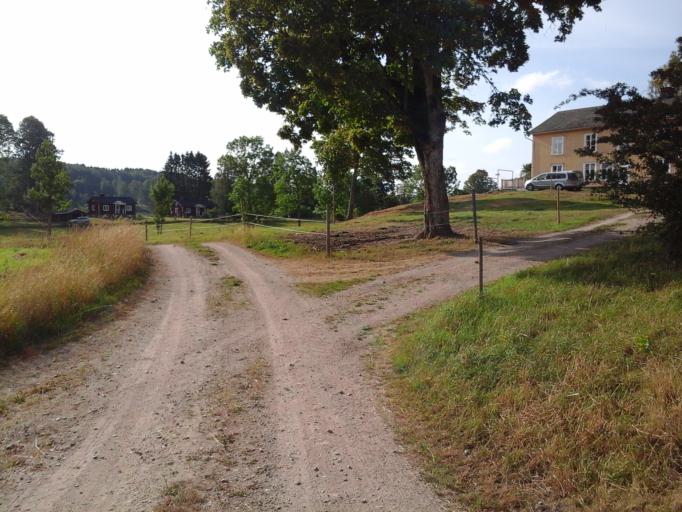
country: SE
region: Vaestra Goetaland
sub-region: Amals Kommun
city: Amal
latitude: 58.9099
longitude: 12.5410
